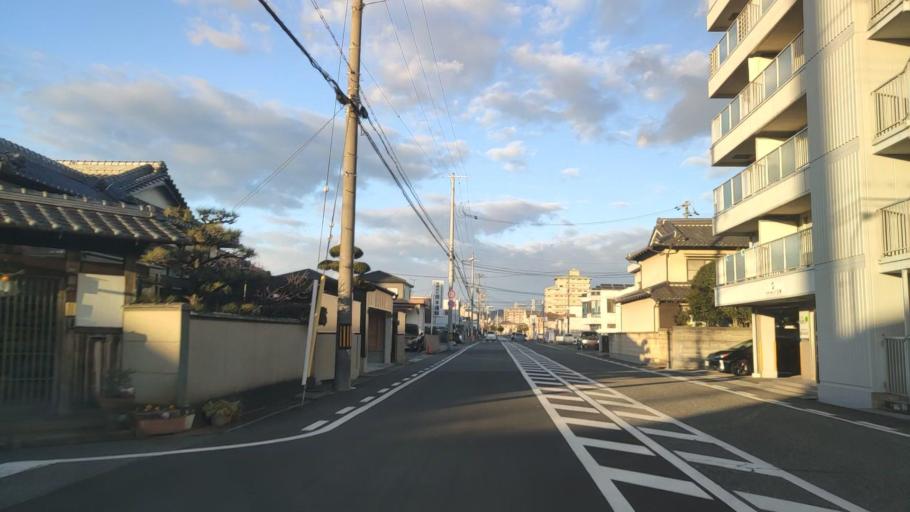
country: JP
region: Hyogo
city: Himeji
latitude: 34.8112
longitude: 134.6880
